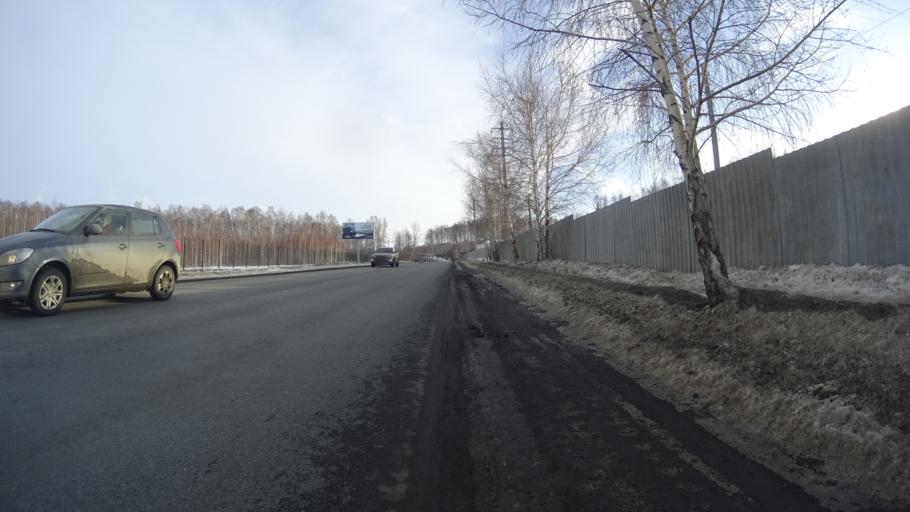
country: RU
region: Chelyabinsk
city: Sargazy
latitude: 55.1306
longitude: 61.2875
